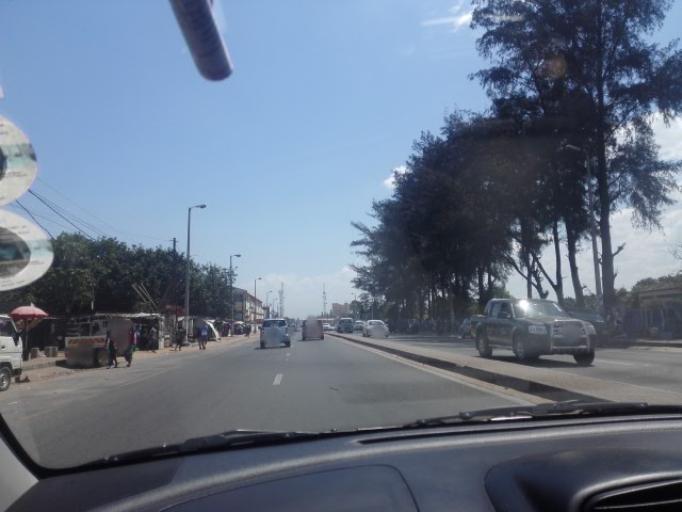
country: MZ
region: Maputo City
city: Maputo
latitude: -25.9317
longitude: 32.5532
